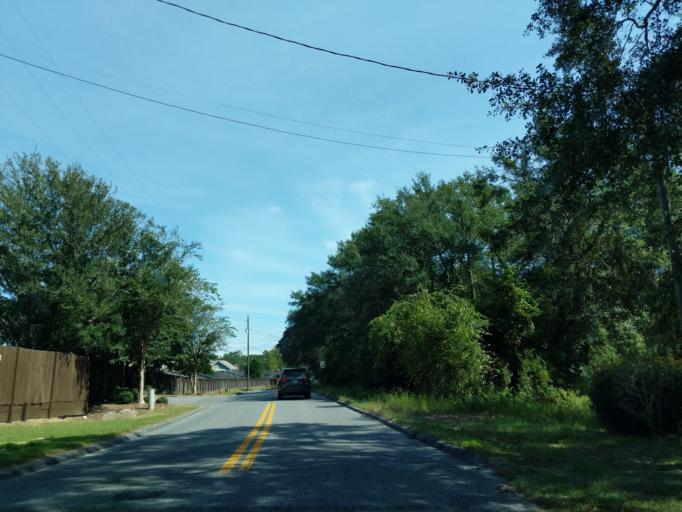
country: US
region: Florida
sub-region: Okaloosa County
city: Crestview
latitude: 30.7046
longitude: -86.5854
